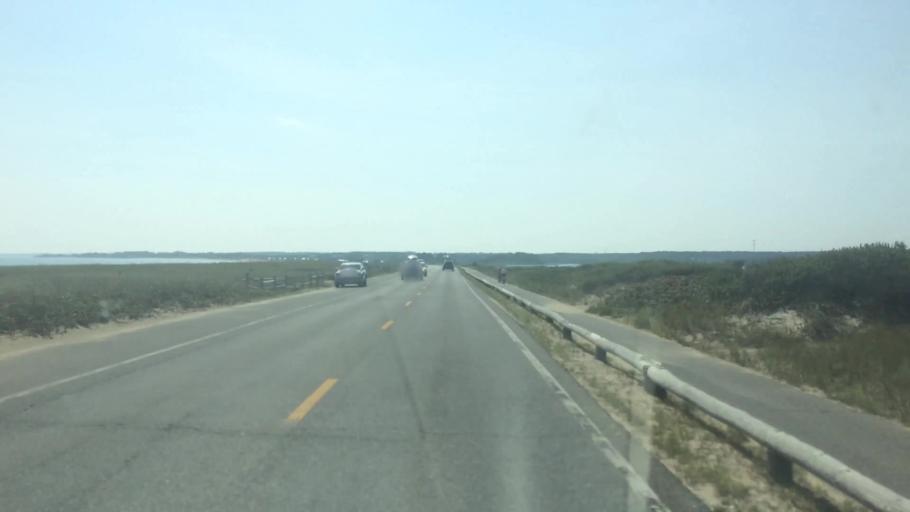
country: US
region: Massachusetts
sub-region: Dukes County
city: Oak Bluffs
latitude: 41.4147
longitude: -70.5473
